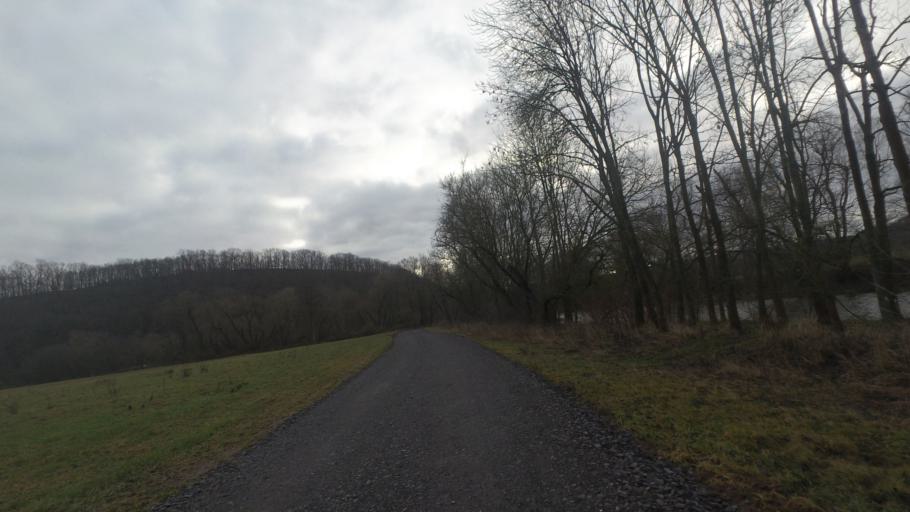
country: DE
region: Thuringia
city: Orlamunde
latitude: 50.7687
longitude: 11.5206
